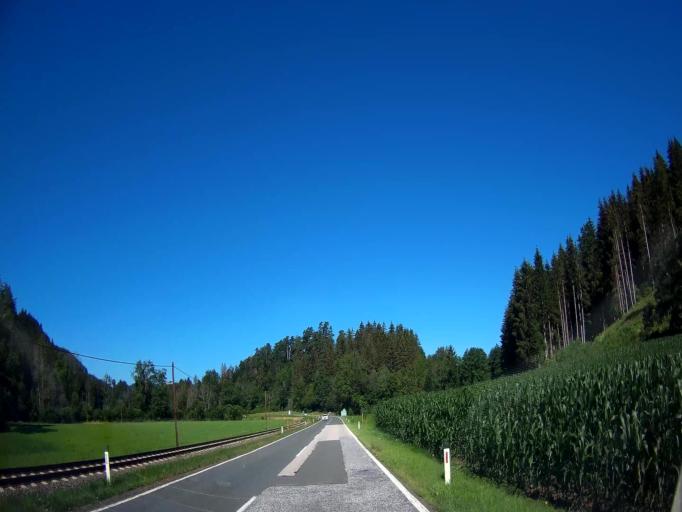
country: AT
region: Carinthia
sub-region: Politischer Bezirk Sankt Veit an der Glan
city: Bruckl
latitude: 46.7619
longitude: 14.4919
